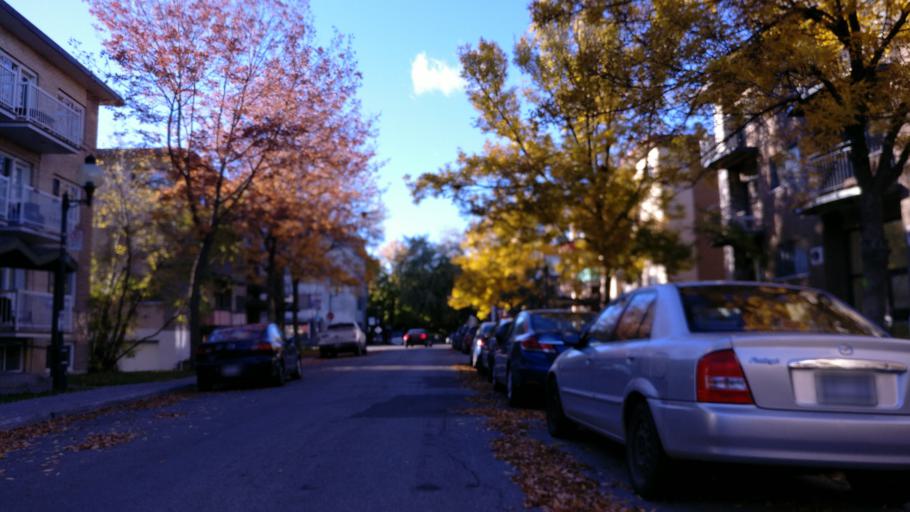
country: CA
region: Quebec
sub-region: Montreal
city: Montreal
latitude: 45.5343
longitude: -73.5648
